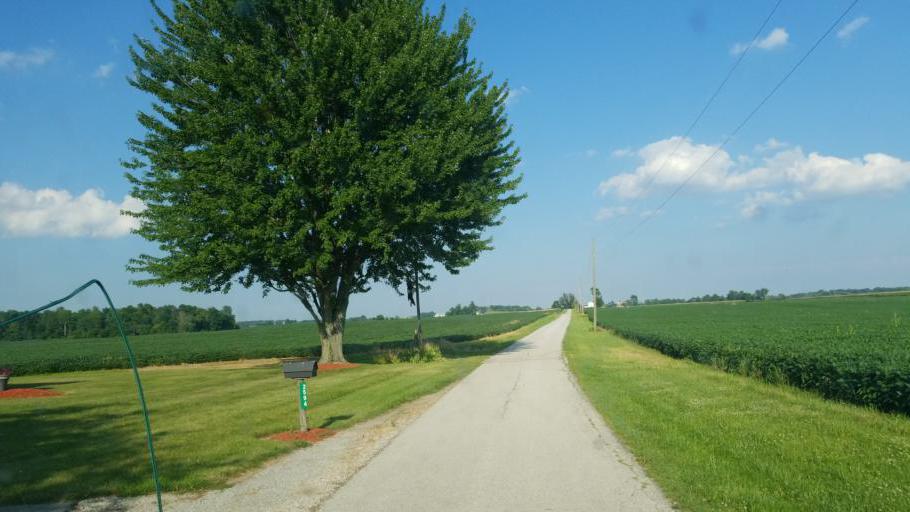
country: US
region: Ohio
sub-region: Crawford County
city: Bucyrus
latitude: 40.8441
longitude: -82.9883
